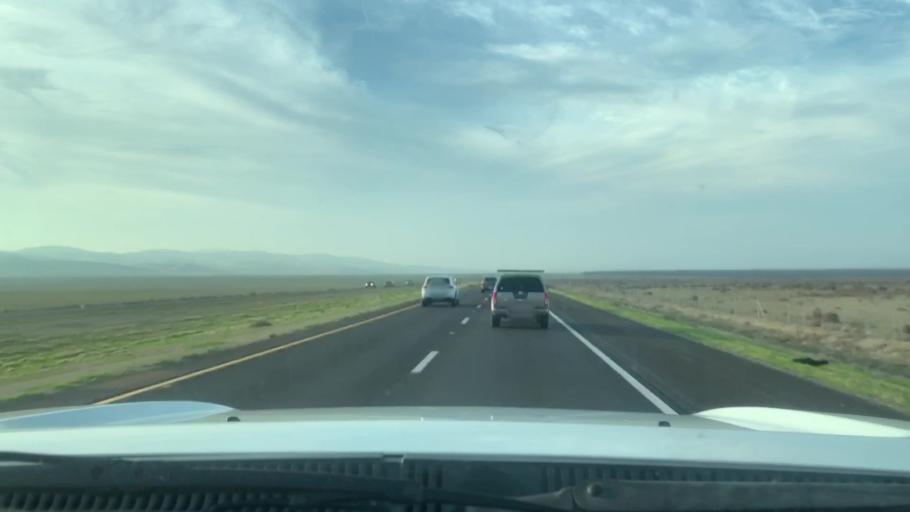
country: US
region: California
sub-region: Kern County
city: Lost Hills
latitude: 35.6230
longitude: -119.9820
